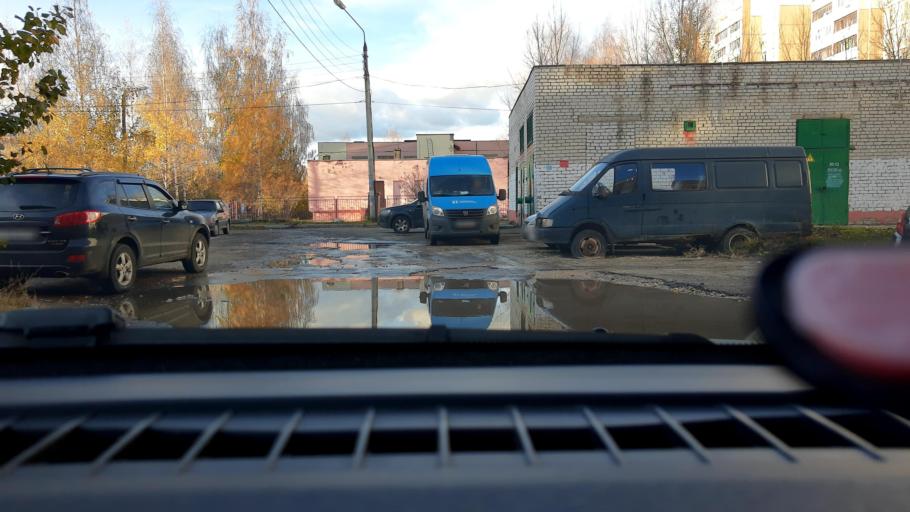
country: RU
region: Nizjnij Novgorod
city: Gorbatovka
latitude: 56.3681
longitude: 43.8076
